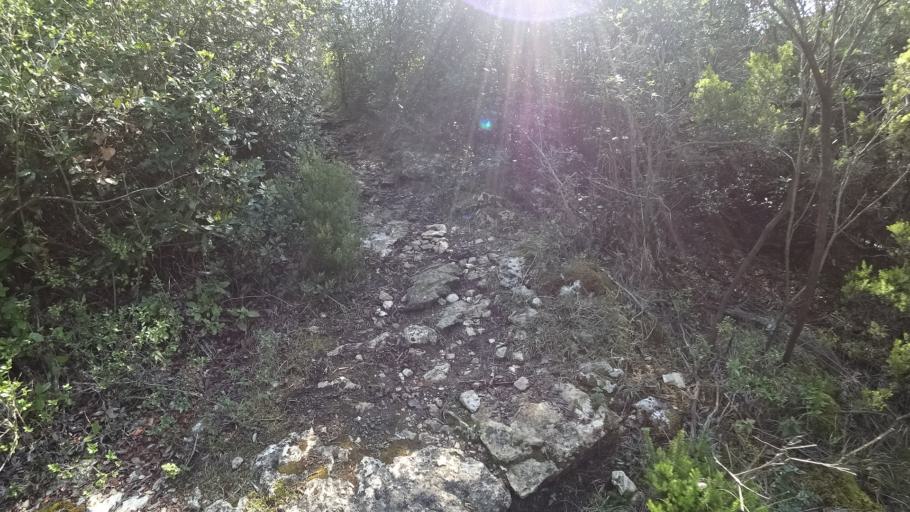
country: HR
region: Primorsko-Goranska
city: Mali Losinj
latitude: 44.5010
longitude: 14.5237
